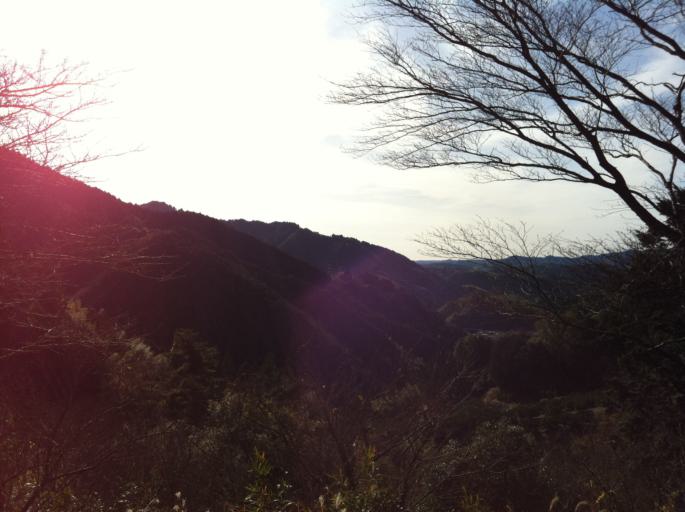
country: JP
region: Shizuoka
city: Yaizu
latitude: 34.9335
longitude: 138.3104
